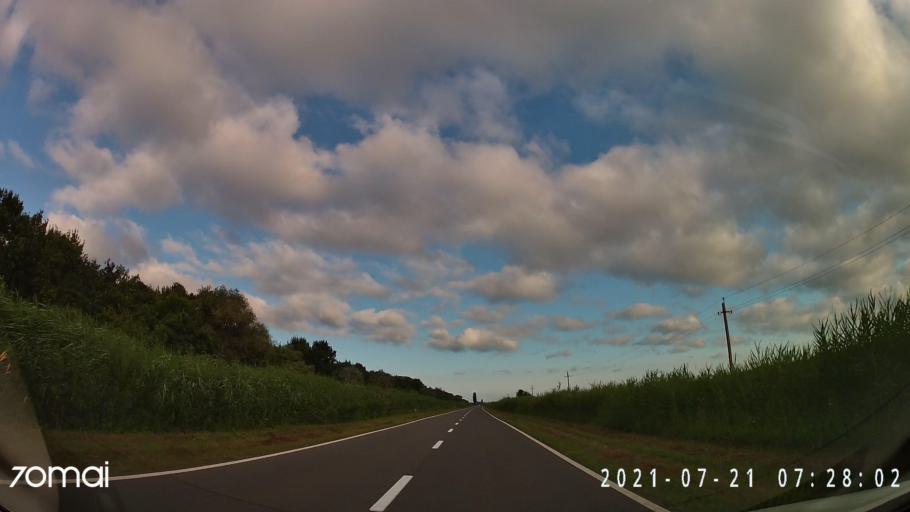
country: RO
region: Tulcea
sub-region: Oras Isaccea
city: Isaccea
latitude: 45.3079
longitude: 28.4026
